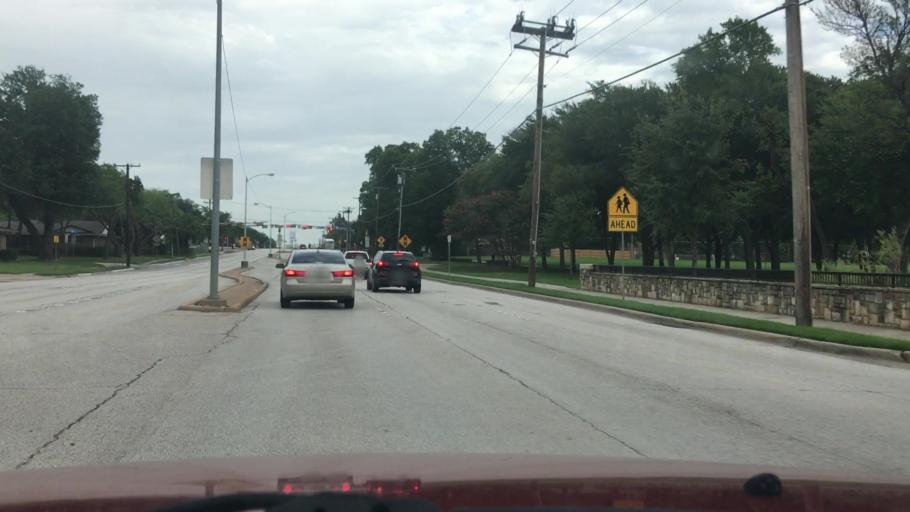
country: US
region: Texas
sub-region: Dallas County
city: Richardson
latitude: 32.9512
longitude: -96.7661
